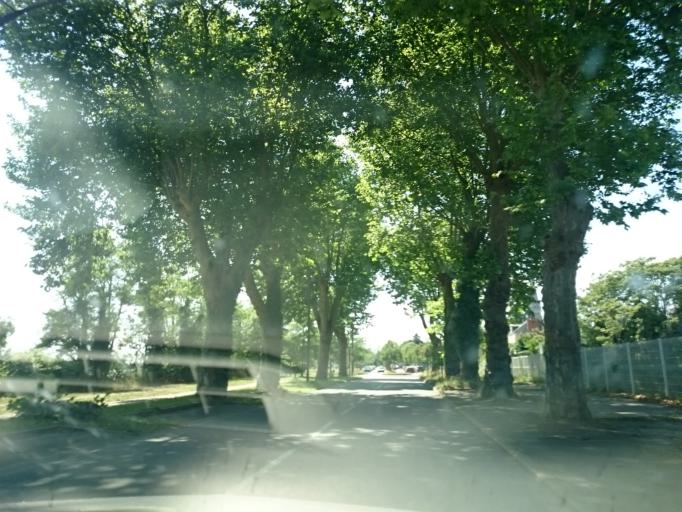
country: FR
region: Pays de la Loire
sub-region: Departement de la Loire-Atlantique
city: Coueron
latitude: 47.2089
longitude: -1.7238
